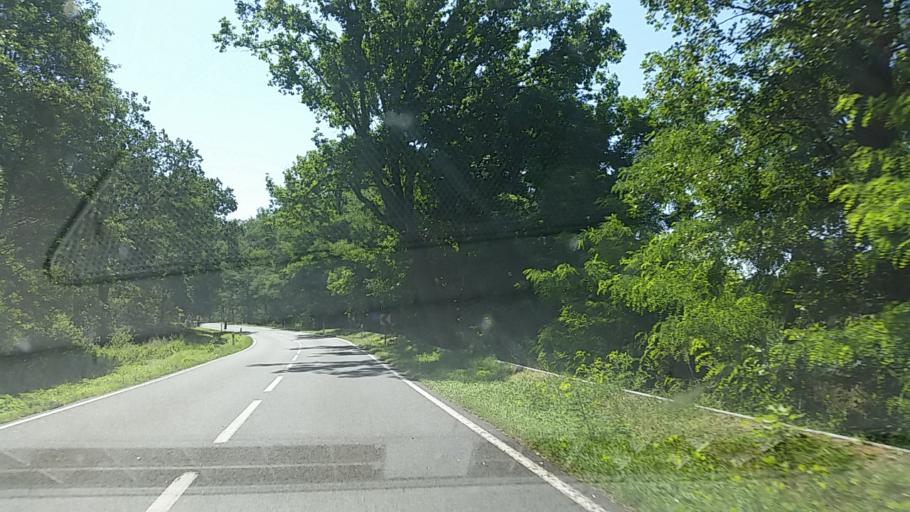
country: DE
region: Saxony-Anhalt
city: Pretzsch
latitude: 51.6812
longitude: 12.8039
